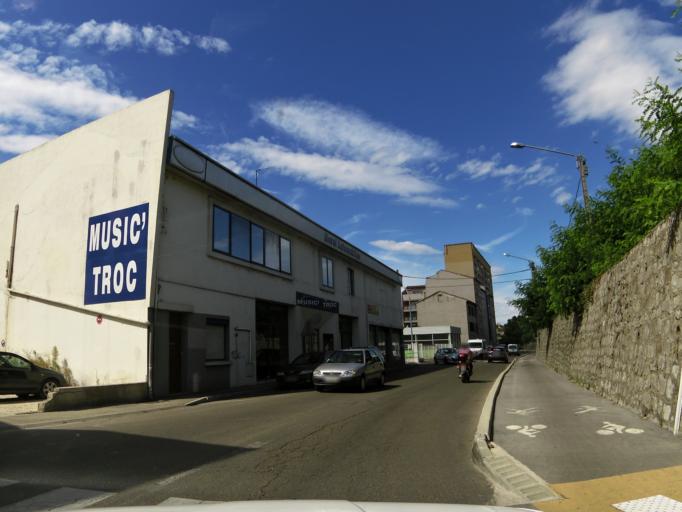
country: FR
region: Languedoc-Roussillon
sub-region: Departement du Gard
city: Ales
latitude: 44.1217
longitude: 4.0921
